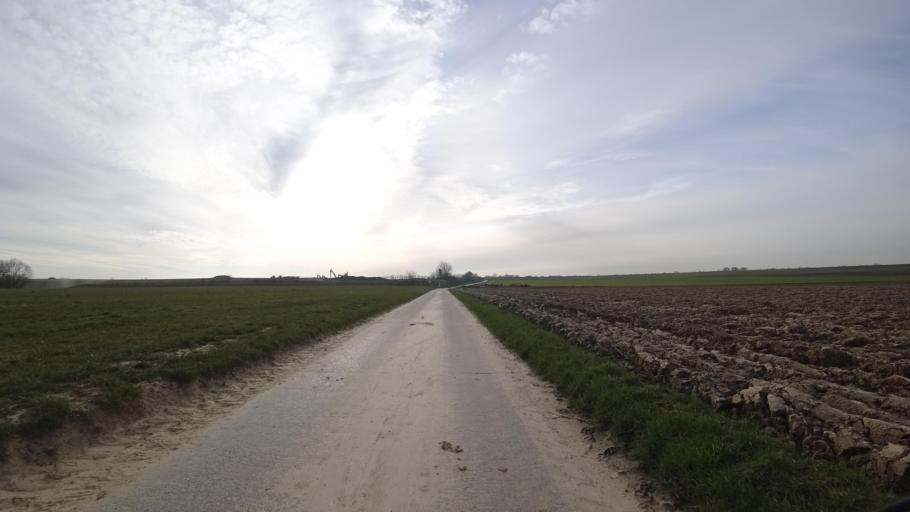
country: BE
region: Wallonia
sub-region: Province du Brabant Wallon
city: Chaumont-Gistoux
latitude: 50.6689
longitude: 4.7102
